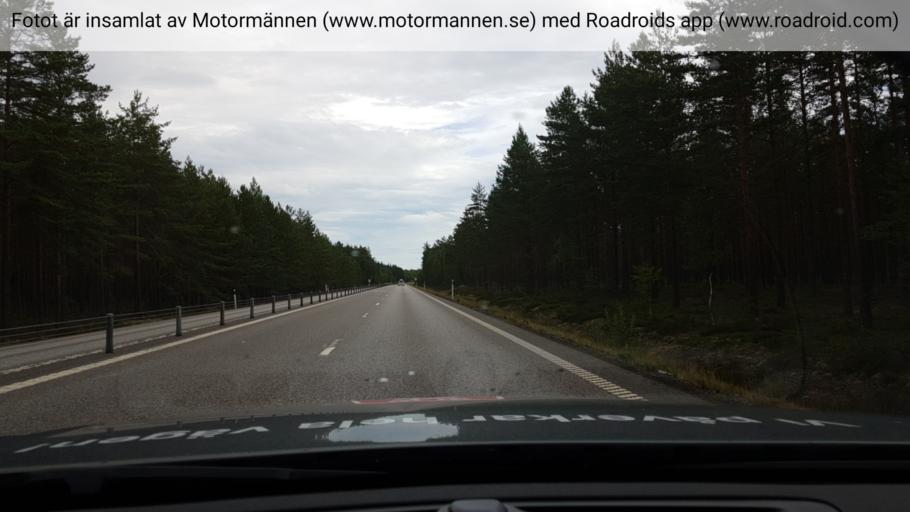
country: SE
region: Uppsala
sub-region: Heby Kommun
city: Tarnsjo
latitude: 60.1382
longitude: 16.9215
